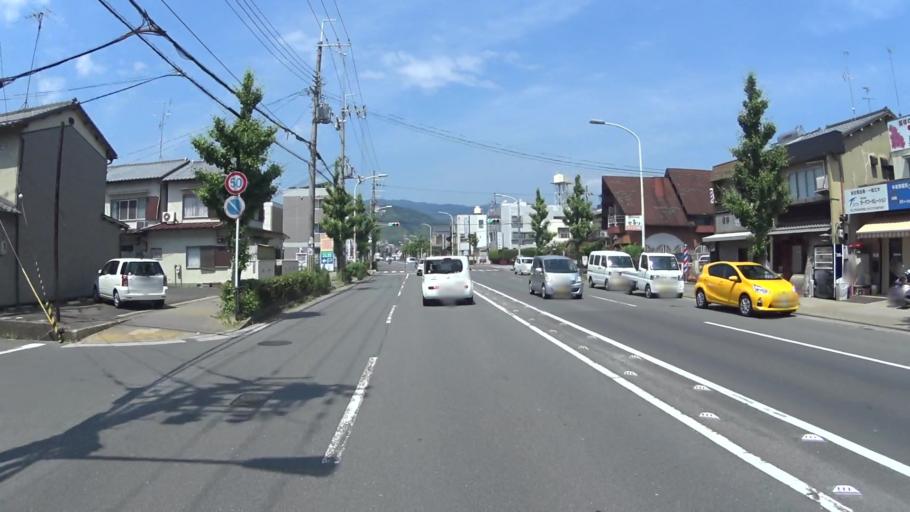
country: JP
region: Kyoto
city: Muko
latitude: 34.9321
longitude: 135.6975
